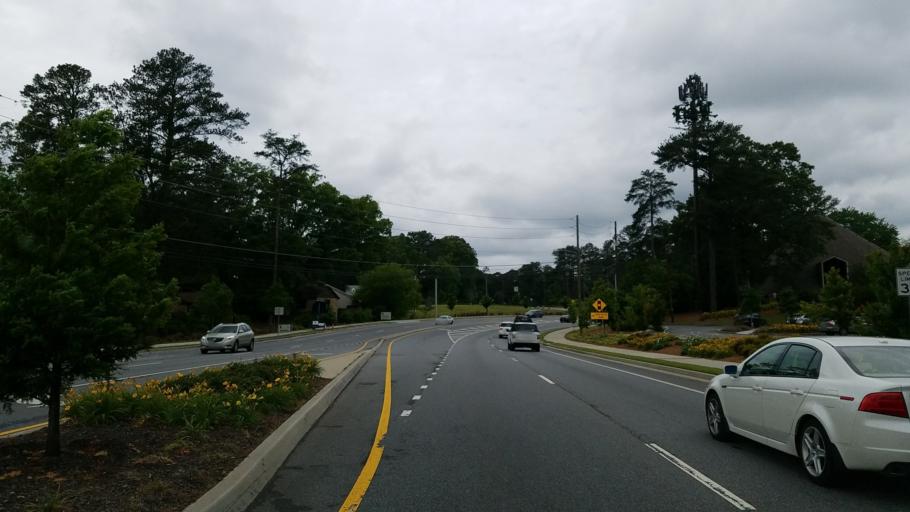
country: US
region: Georgia
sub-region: Fulton County
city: Sandy Springs
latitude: 33.9356
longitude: -84.3901
